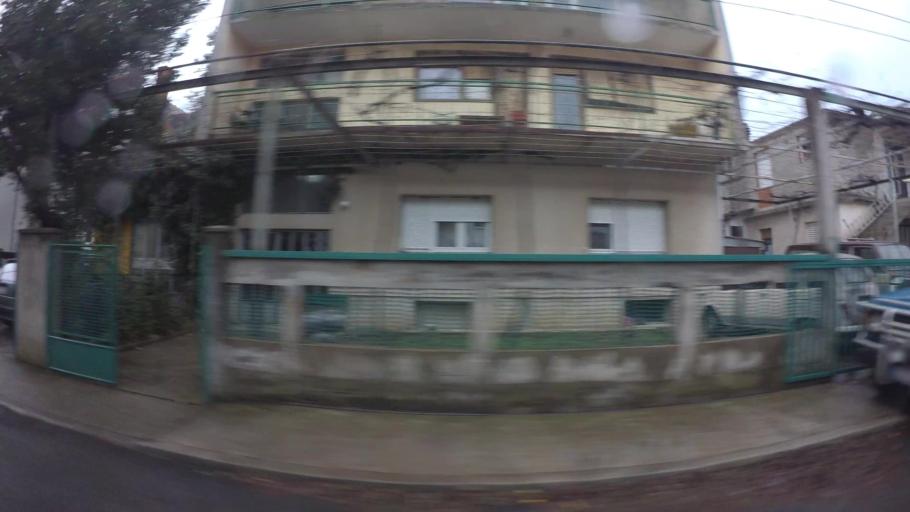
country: BA
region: Federation of Bosnia and Herzegovina
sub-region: Hercegovacko-Bosanski Kanton
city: Mostar
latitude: 43.3573
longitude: 17.8026
